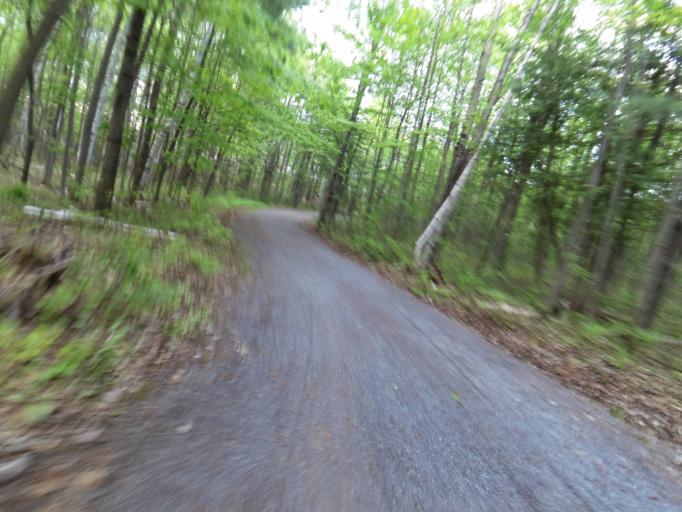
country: CA
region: Ontario
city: Bells Corners
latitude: 45.3263
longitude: -75.8597
